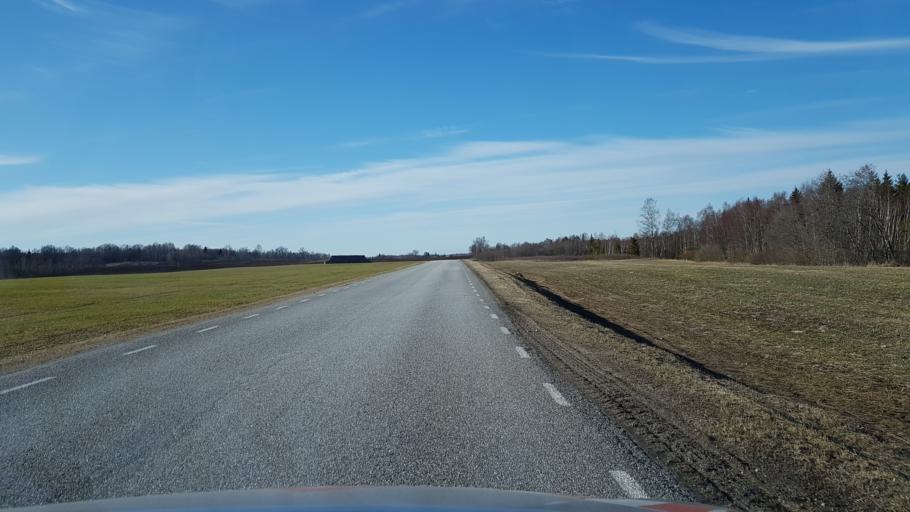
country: EE
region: Laeaene-Virumaa
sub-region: Kadrina vald
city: Kadrina
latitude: 59.2991
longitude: 26.1639
